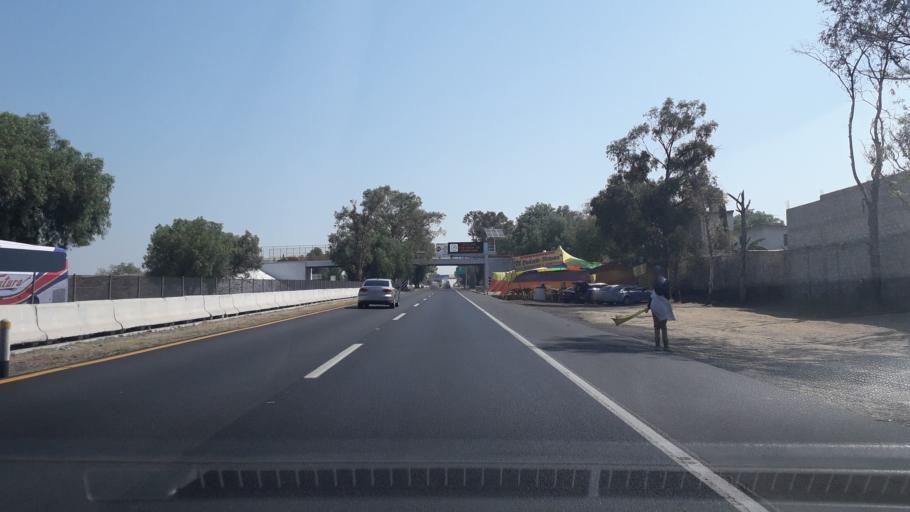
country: MX
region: Mexico
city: Santo Tomas Chiconautla
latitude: 19.6529
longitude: -99.0113
